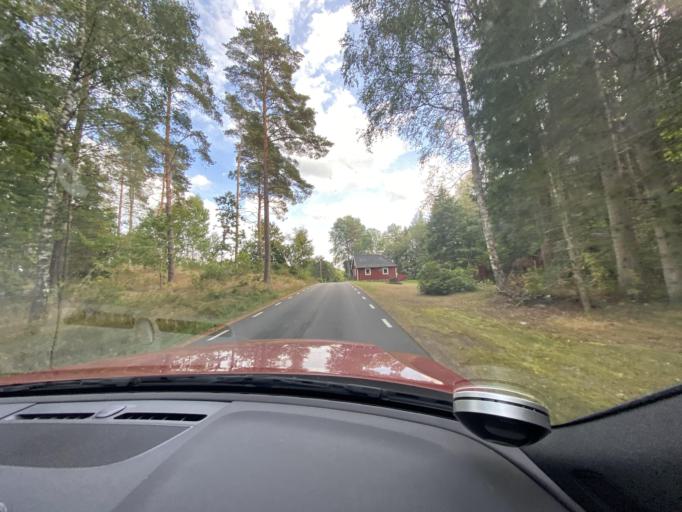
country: SE
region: Skane
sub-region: Hassleholms Kommun
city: Bjarnum
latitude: 56.3573
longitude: 13.8062
